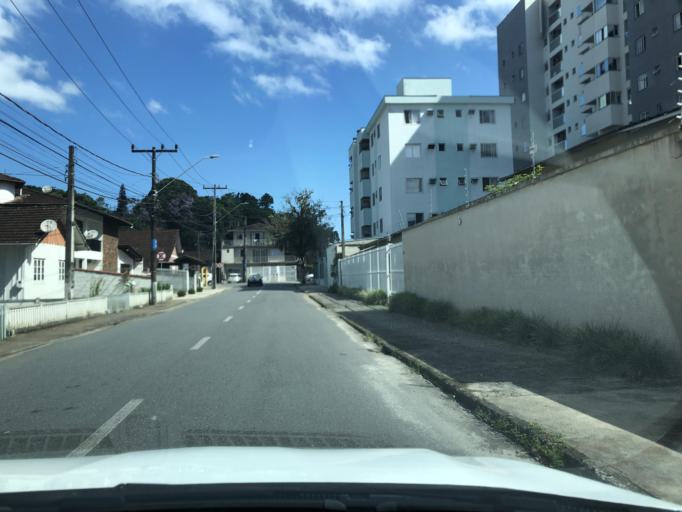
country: BR
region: Santa Catarina
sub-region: Joinville
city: Joinville
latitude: -26.2700
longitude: -48.8466
